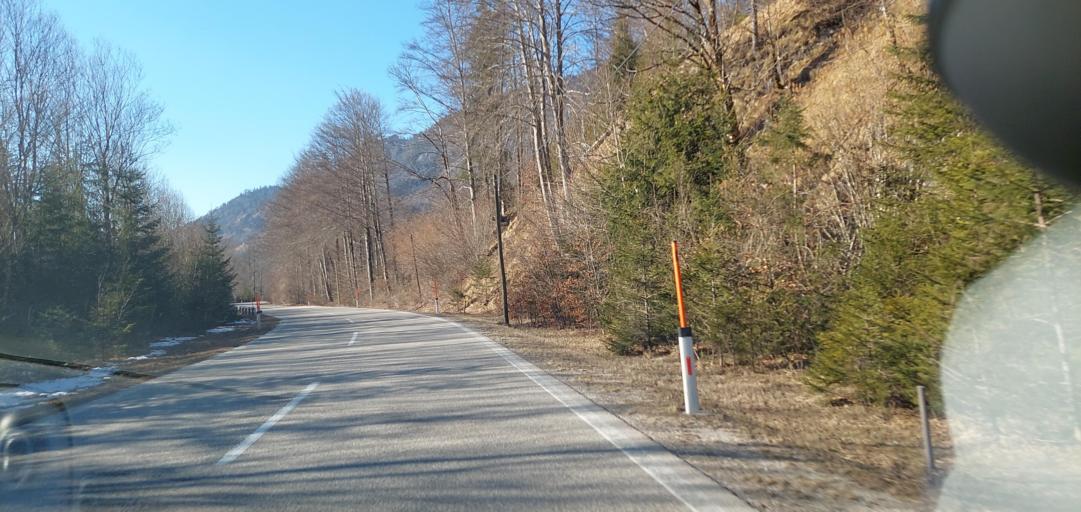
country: AT
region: Upper Austria
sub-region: Politischer Bezirk Vocklabruck
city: Steinbach am Attersee
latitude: 47.7868
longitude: 13.5836
